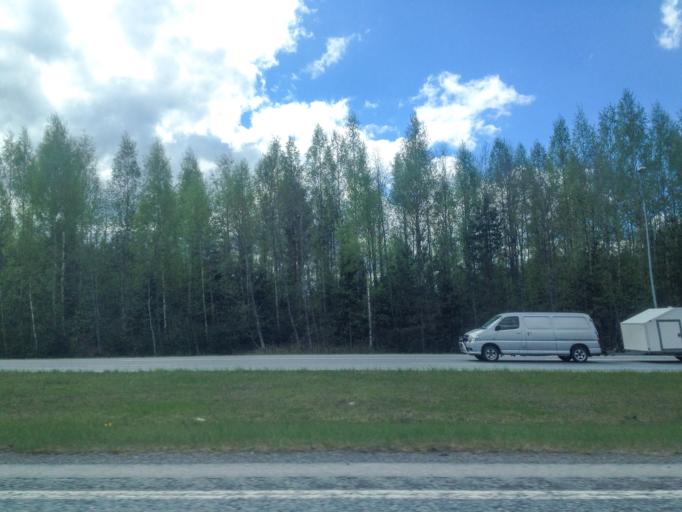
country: FI
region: Haeme
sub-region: Haemeenlinna
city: Janakkala
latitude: 60.9133
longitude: 24.5409
